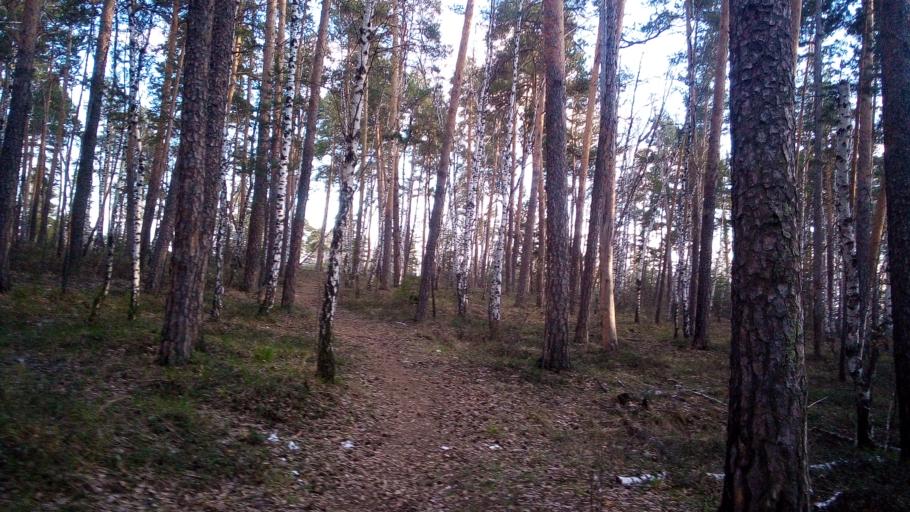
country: RU
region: Chelyabinsk
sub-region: Gorod Chelyabinsk
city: Chelyabinsk
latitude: 55.1608
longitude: 61.3230
